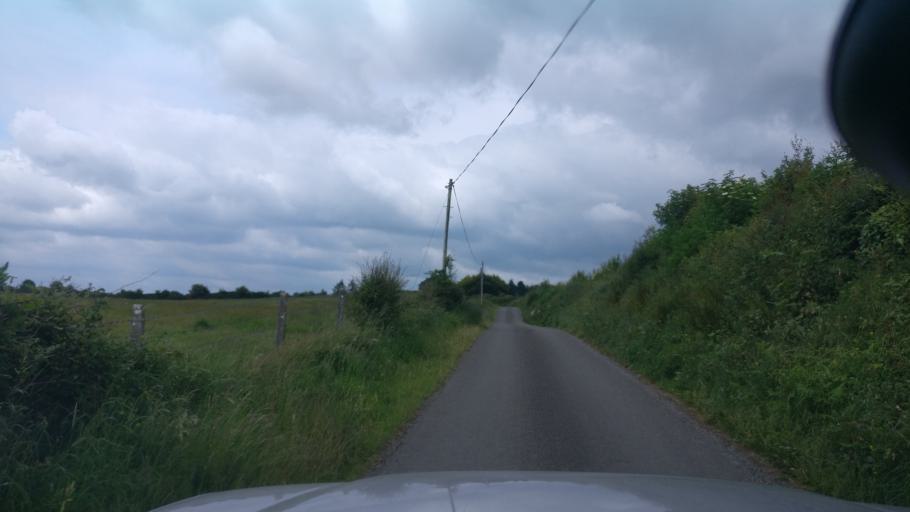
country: IE
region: Connaught
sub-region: County Galway
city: Ballinasloe
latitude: 53.2888
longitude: -8.3173
